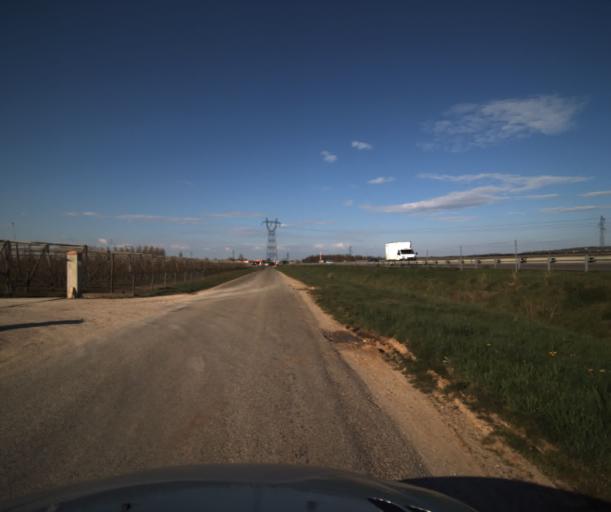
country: FR
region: Midi-Pyrenees
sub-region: Departement du Tarn-et-Garonne
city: Bressols
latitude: 43.9542
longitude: 1.3261
